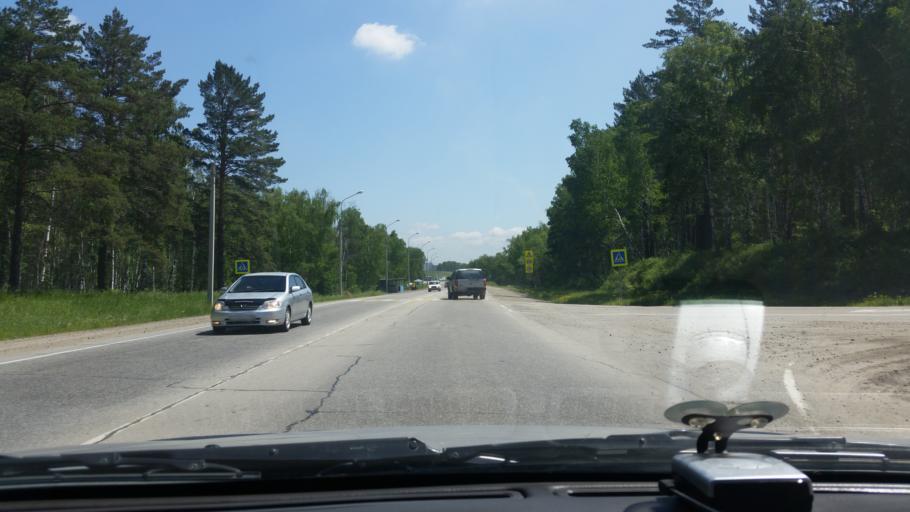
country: RU
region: Irkutsk
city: Smolenshchina
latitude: 52.2523
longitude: 104.1631
